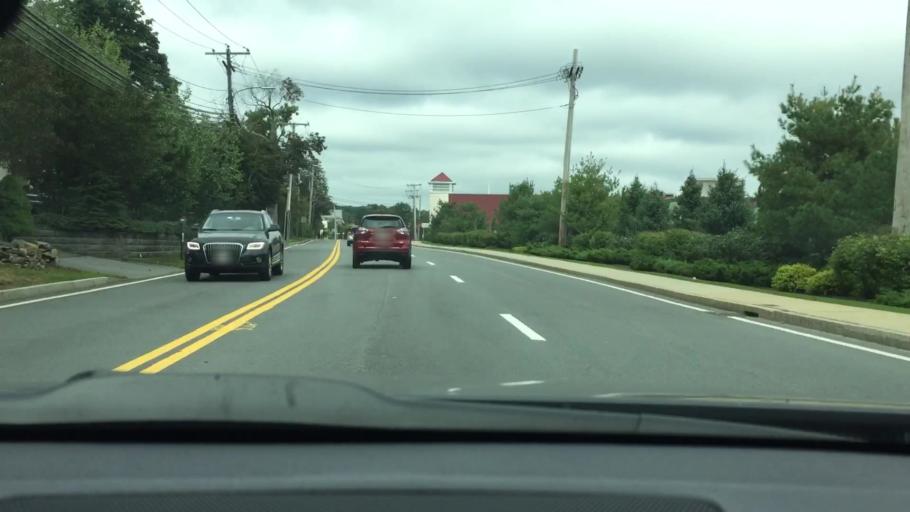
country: US
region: Massachusetts
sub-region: Norfolk County
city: Dedham
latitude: 42.2301
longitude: -71.1782
